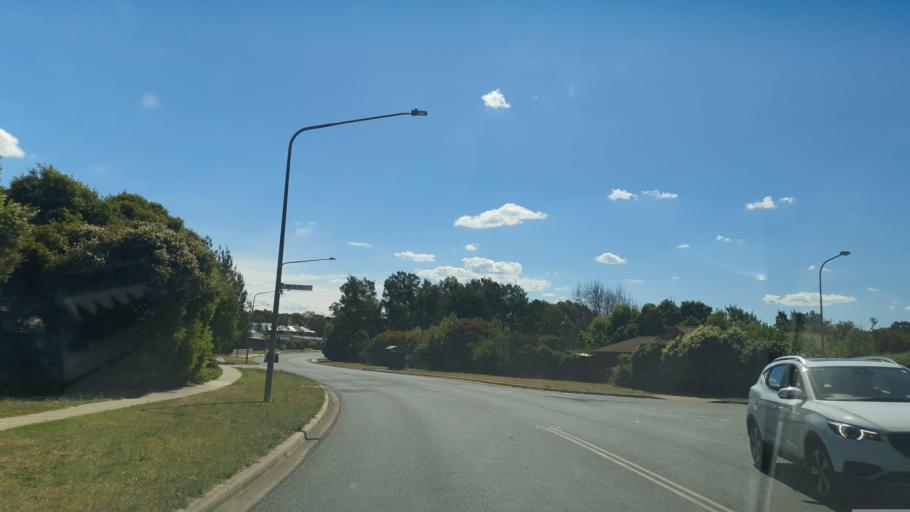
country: AU
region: Australian Capital Territory
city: Belconnen
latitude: -35.2258
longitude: 149.0593
